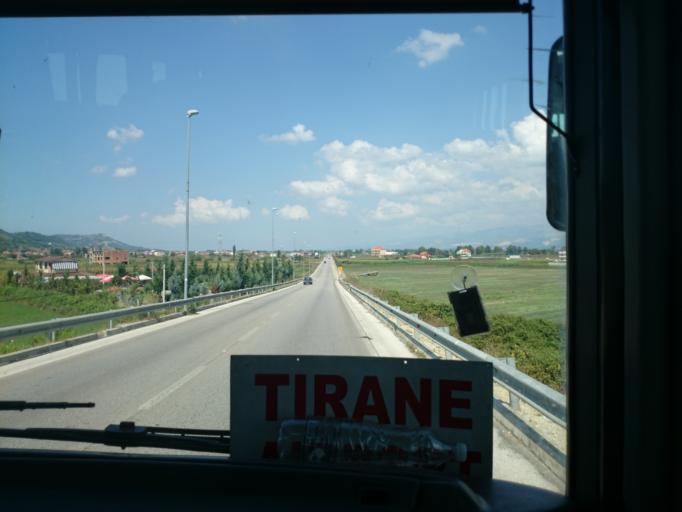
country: AL
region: Tirane
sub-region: Rrethi i Tiranes
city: Berxull
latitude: 41.3720
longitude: 19.7035
